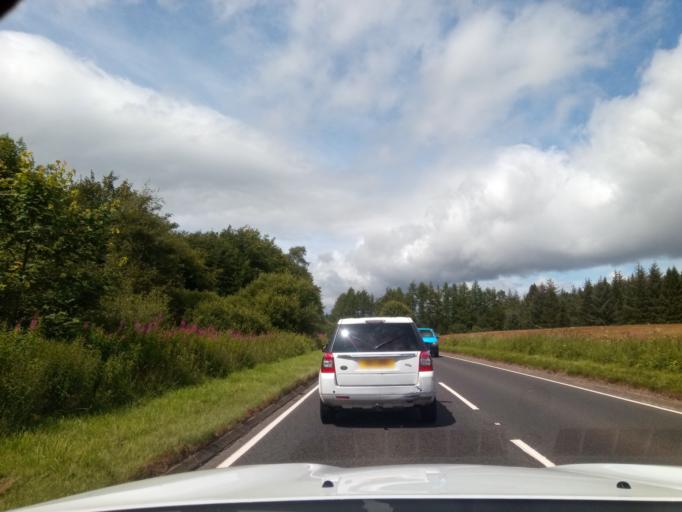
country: GB
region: Scotland
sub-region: Stirling
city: Callander
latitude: 56.2221
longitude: -4.1648
